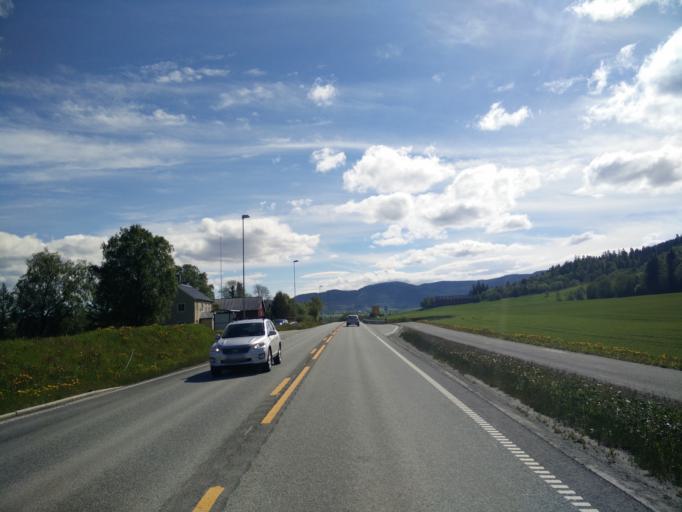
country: NO
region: Sor-Trondelag
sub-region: Melhus
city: Melhus
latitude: 63.3229
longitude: 10.2525
